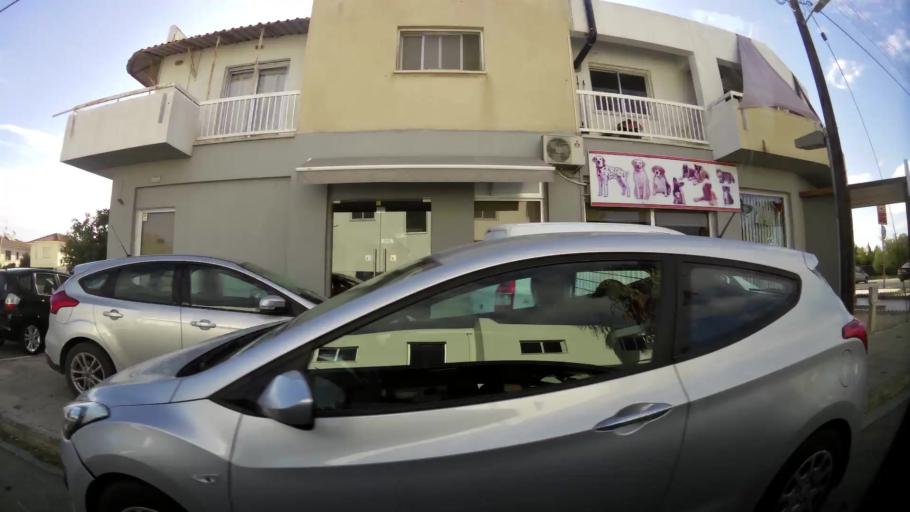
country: CY
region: Lefkosia
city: Nicosia
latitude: 35.1325
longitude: 33.3597
